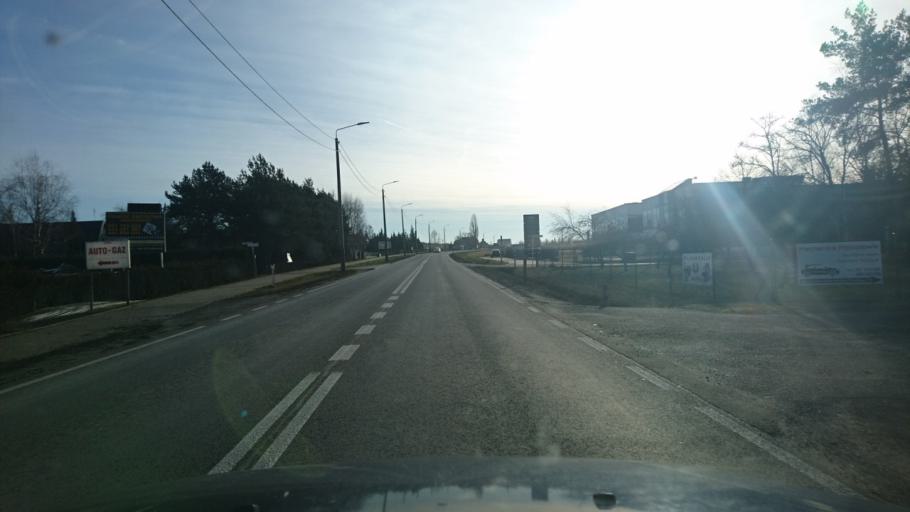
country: PL
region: Greater Poland Voivodeship
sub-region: Powiat ostrzeszowski
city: Ostrzeszow
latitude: 51.4439
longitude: 17.9125
